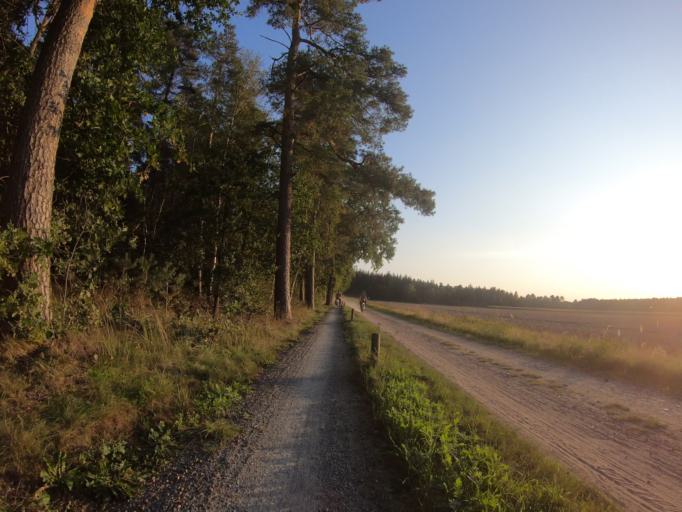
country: DE
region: Lower Saxony
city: Calberlah
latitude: 52.4673
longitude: 10.6218
